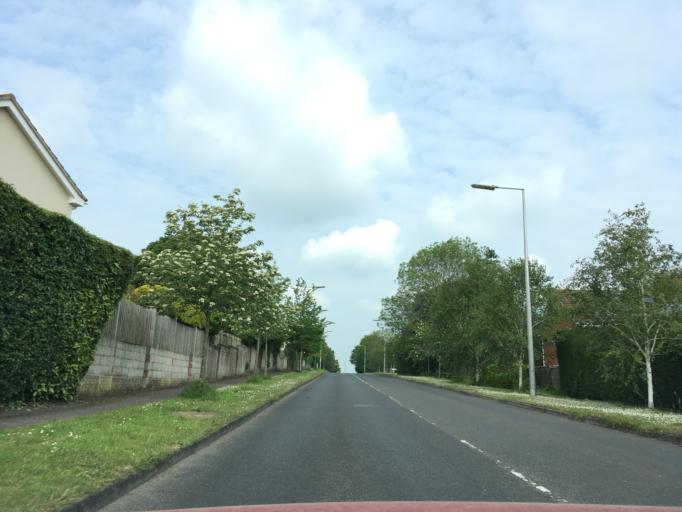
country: GB
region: England
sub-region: North Somerset
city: Nailsea
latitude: 51.4251
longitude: -2.7564
